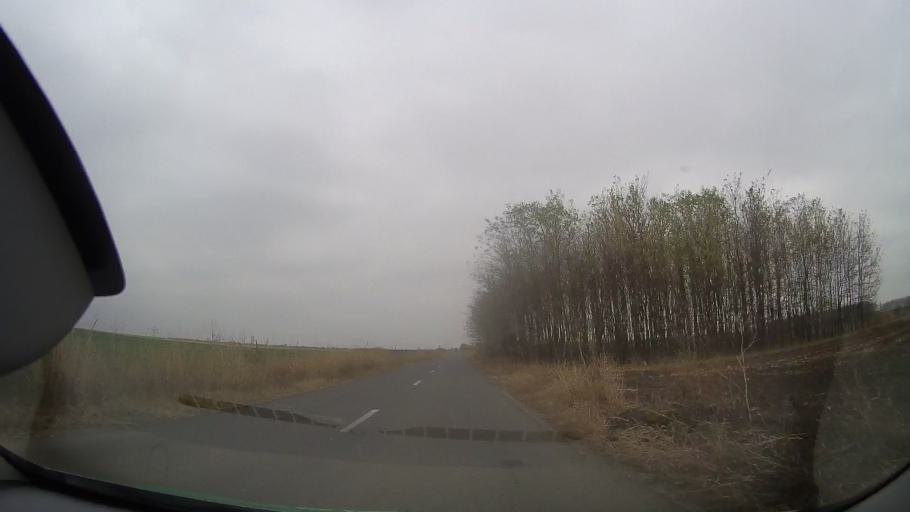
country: RO
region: Buzau
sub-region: Comuna Scutelnici
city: Scutelnici
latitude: 44.8625
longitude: 26.8982
